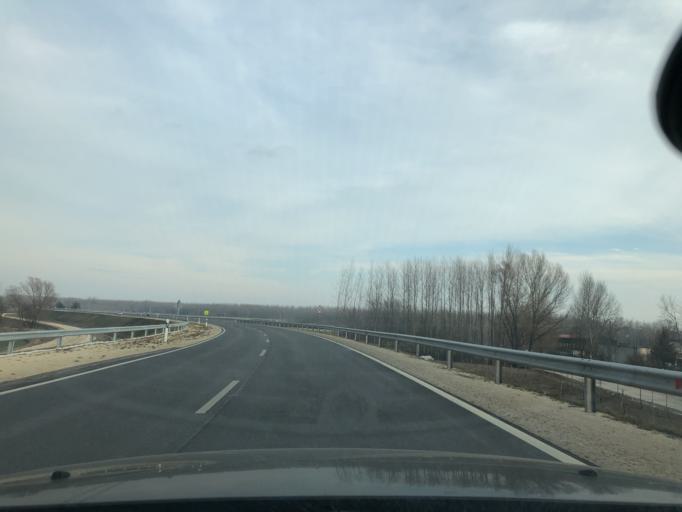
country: HU
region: Gyor-Moson-Sopron
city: Gyor
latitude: 47.7313
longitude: 17.6885
